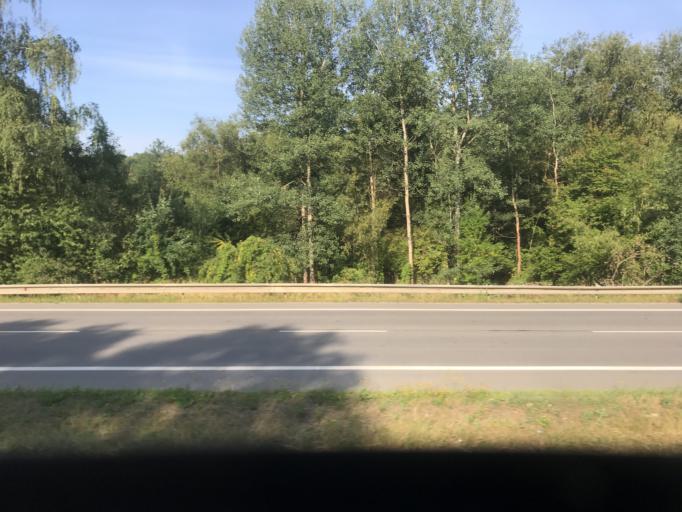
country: CZ
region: Jihocesky
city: Plana nad Luznici
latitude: 49.3397
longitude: 14.7121
